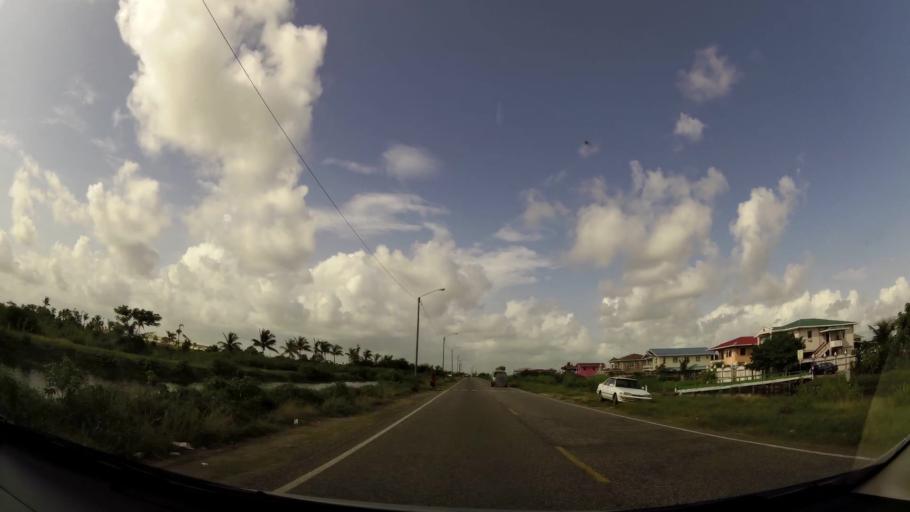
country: GY
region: Demerara-Mahaica
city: Mahaica Village
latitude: 6.7429
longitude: -57.9557
